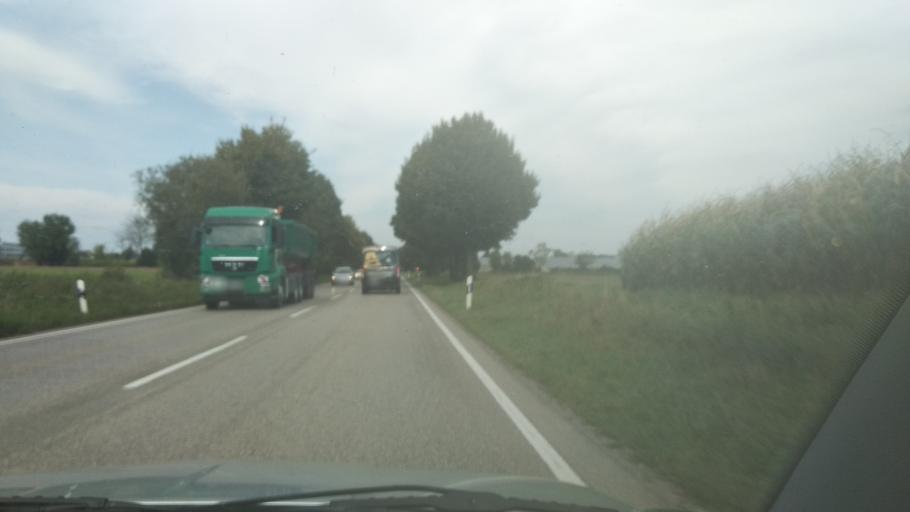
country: DE
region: Bavaria
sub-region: Upper Bavaria
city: Ismaning
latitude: 48.2243
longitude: 11.6896
